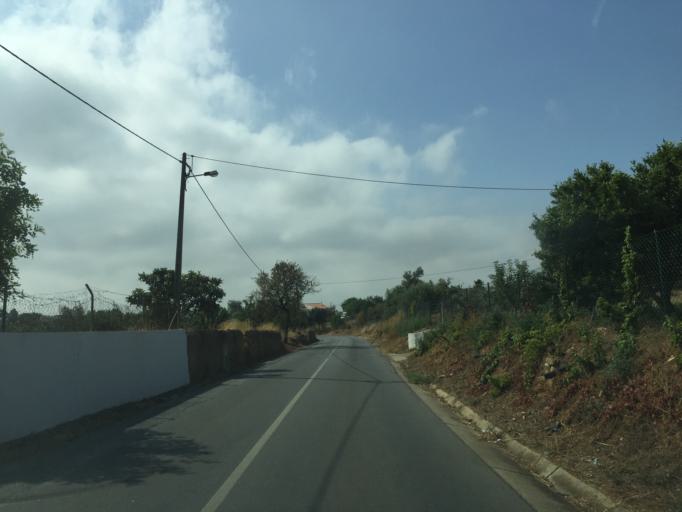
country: PT
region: Faro
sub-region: Olhao
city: Olhao
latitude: 37.0763
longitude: -7.8895
